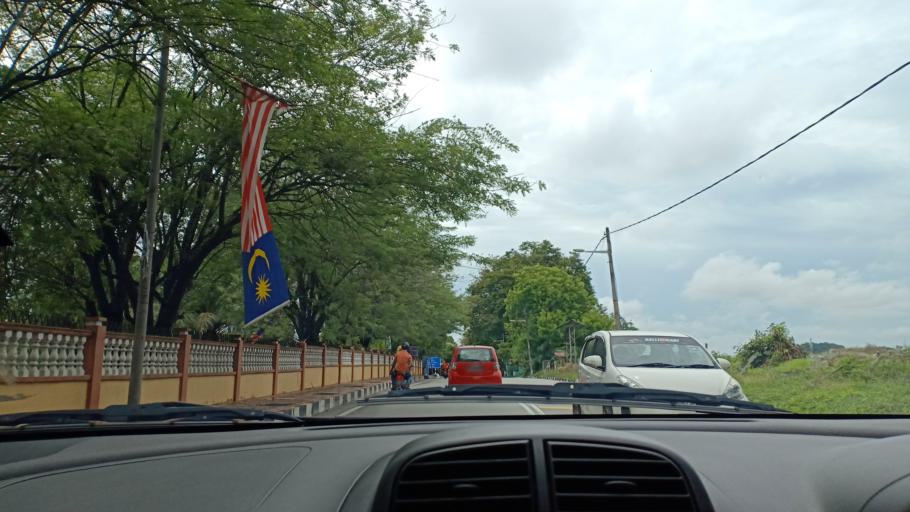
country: MY
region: Penang
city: Bukit Mertajam
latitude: 5.4058
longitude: 100.4686
